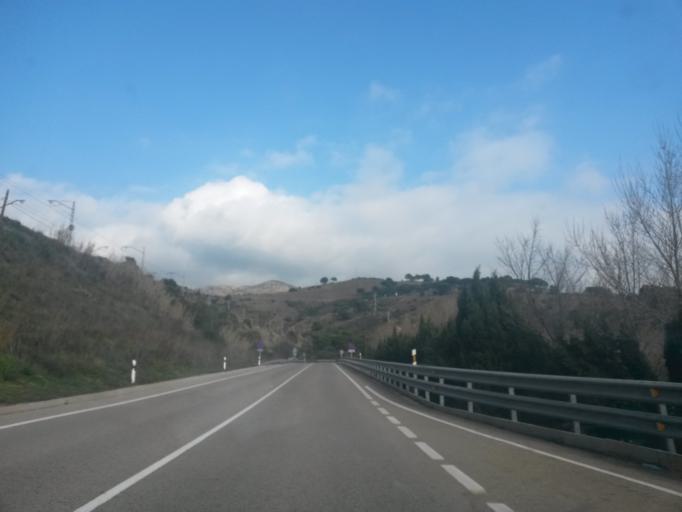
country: ES
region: Catalonia
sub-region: Provincia de Girona
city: Colera
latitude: 42.3939
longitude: 3.1518
